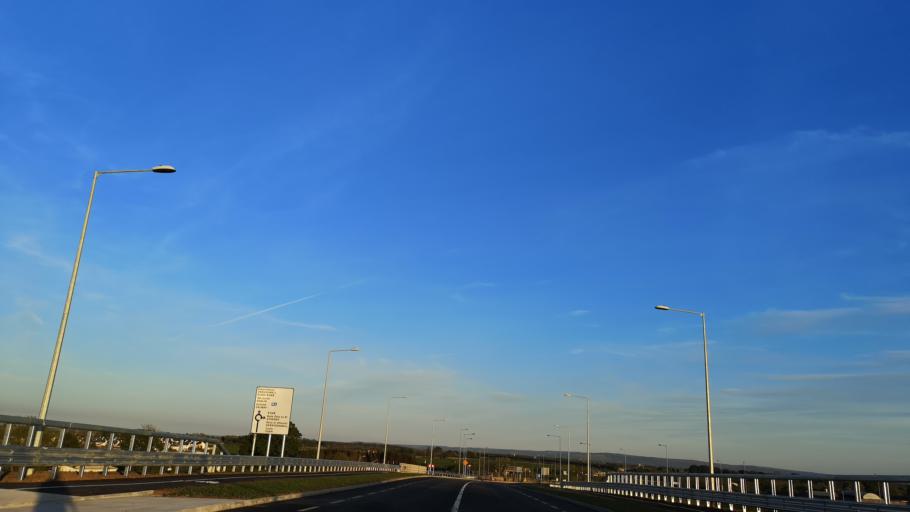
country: IE
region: Connaught
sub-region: County Galway
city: Athenry
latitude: 53.2955
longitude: -8.7604
